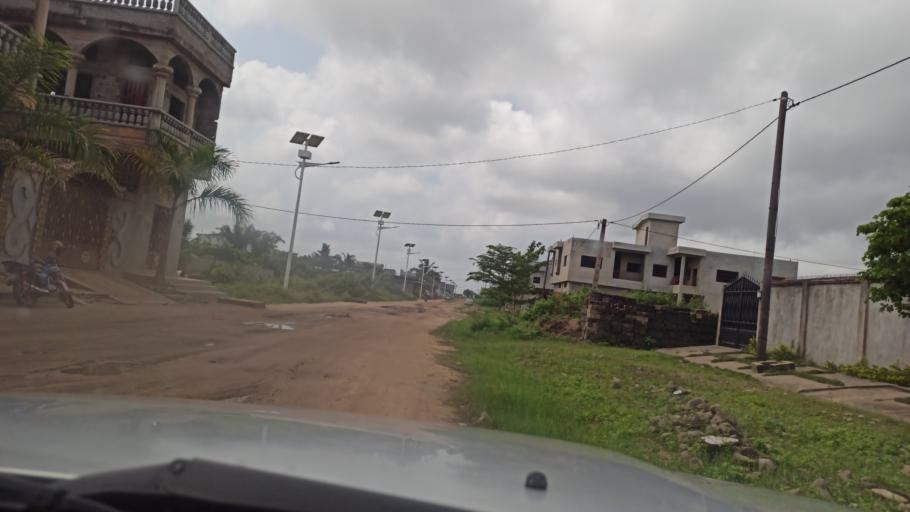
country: BJ
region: Queme
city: Porto-Novo
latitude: 6.4640
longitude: 2.6540
